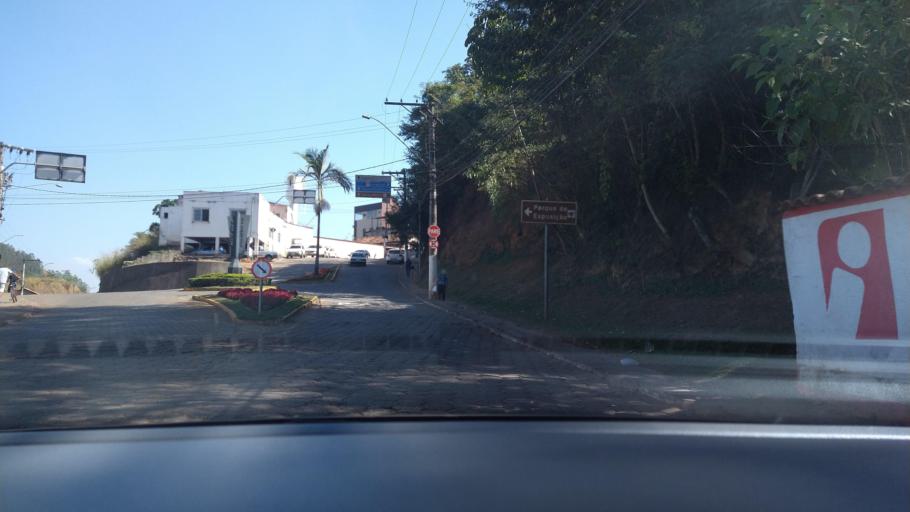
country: BR
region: Minas Gerais
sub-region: Rio Piracicaba
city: Rio Piracicaba
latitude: -19.9282
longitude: -43.1698
